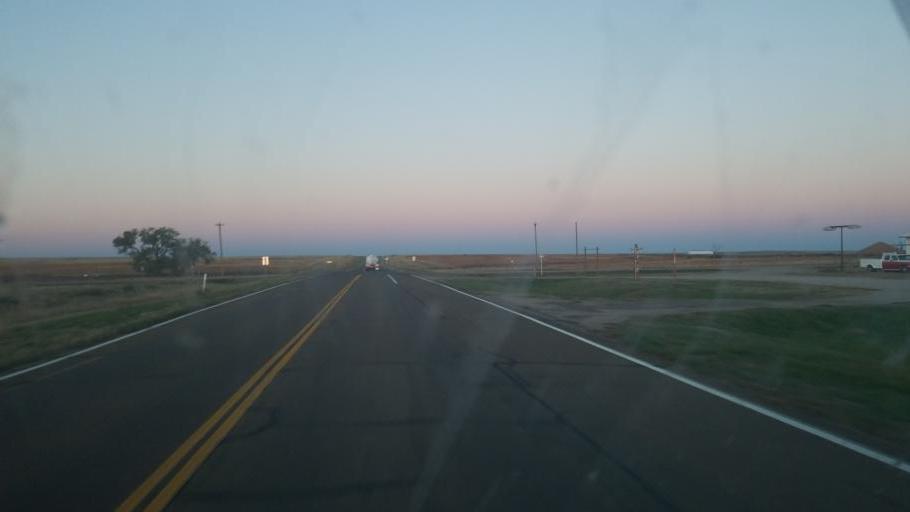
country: US
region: Kansas
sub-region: Wallace County
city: Sharon Springs
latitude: 38.9088
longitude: -101.5906
